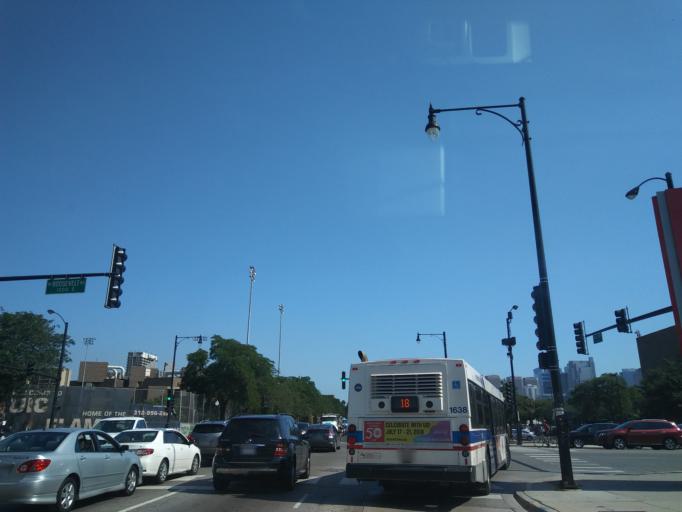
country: US
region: Illinois
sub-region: Cook County
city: Chicago
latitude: 41.8668
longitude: -87.6468
